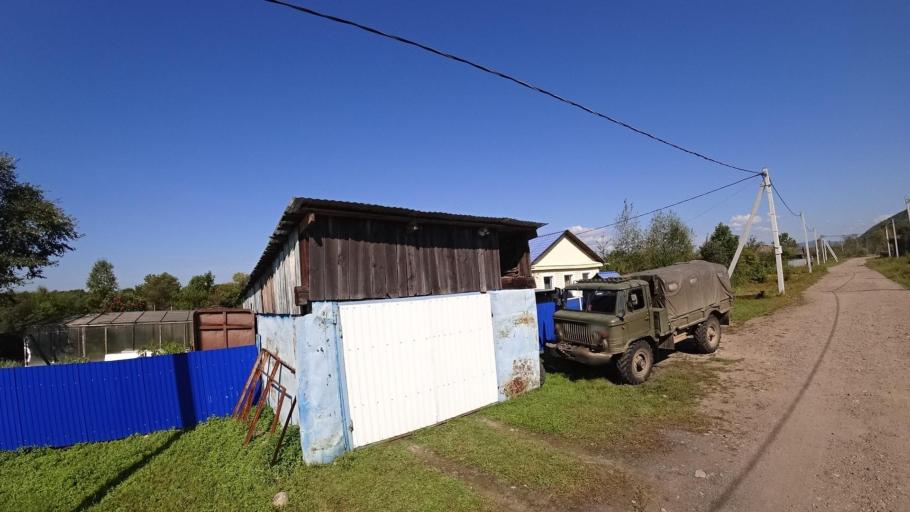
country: RU
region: Jewish Autonomous Oblast
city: Bira
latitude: 48.9986
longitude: 132.4503
